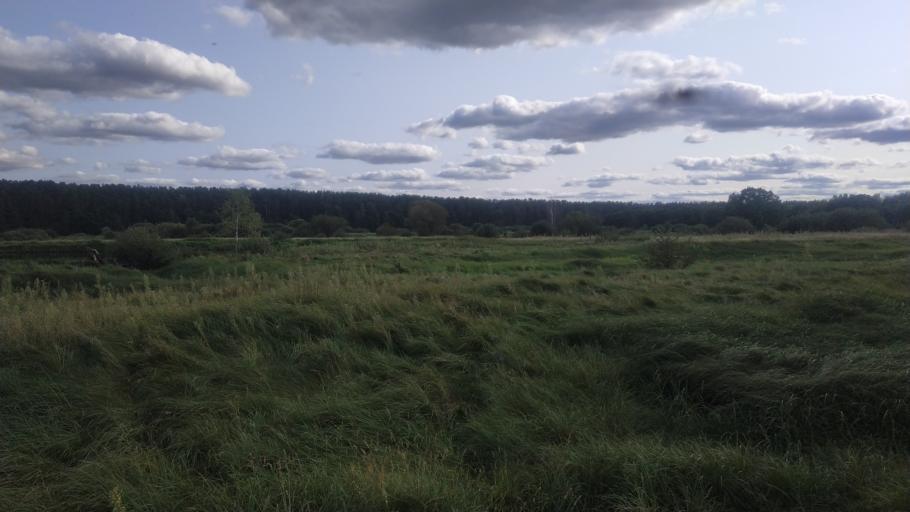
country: RU
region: Brjansk
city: Zhukovka
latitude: 53.5295
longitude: 33.6835
